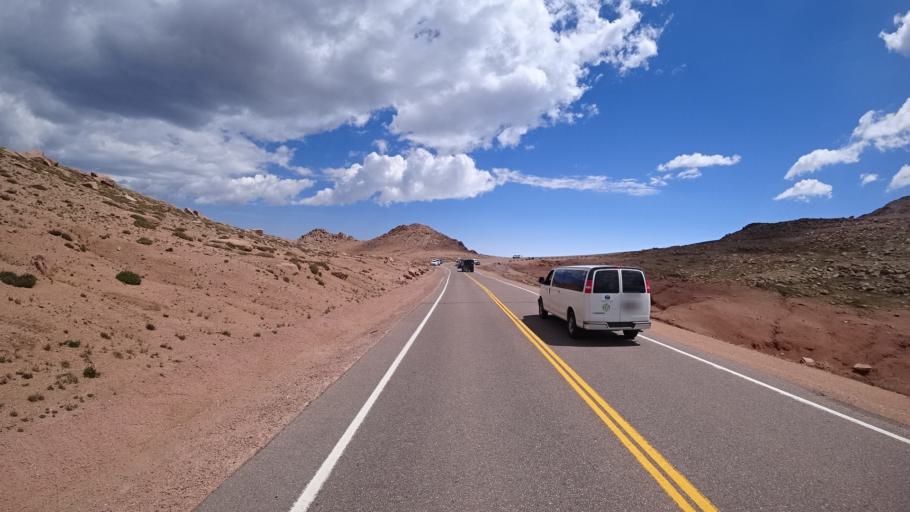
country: US
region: Colorado
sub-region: El Paso County
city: Cascade-Chipita Park
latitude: 38.8484
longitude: -105.0582
